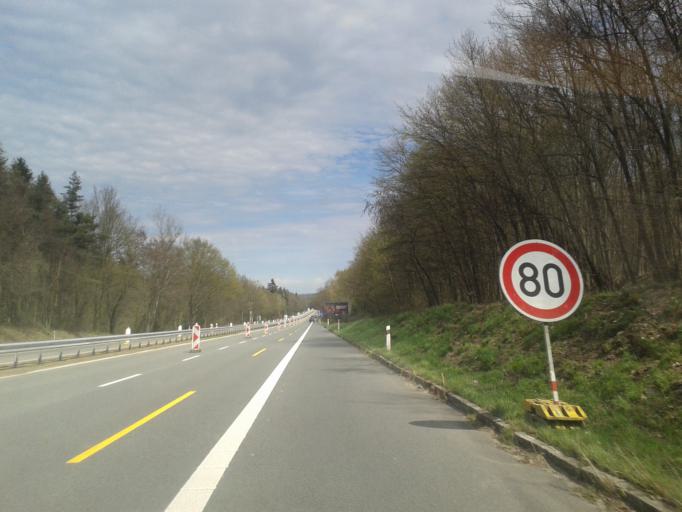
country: CZ
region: Central Bohemia
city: Vrane nad Vltavou
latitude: 49.9379
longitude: 14.3615
